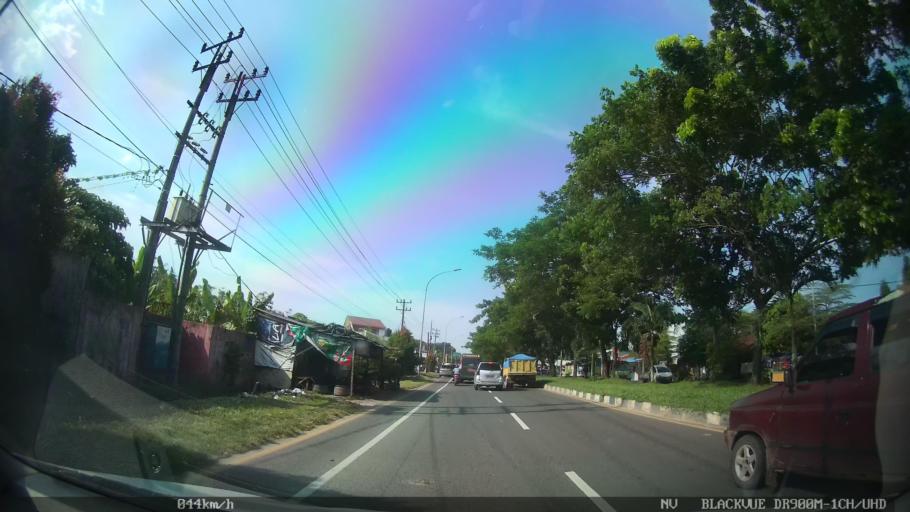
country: ID
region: North Sumatra
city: Percut
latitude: 3.5921
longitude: 98.8060
